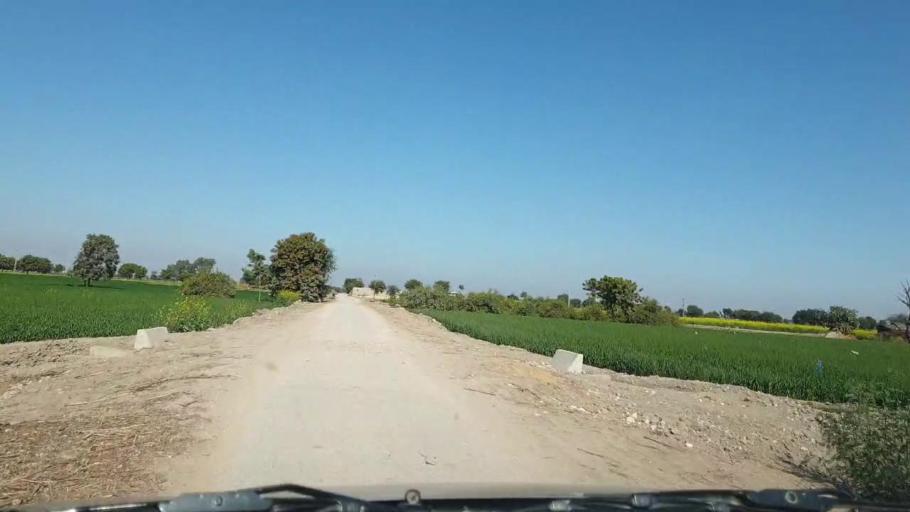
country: PK
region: Sindh
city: Khadro
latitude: 26.1393
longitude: 68.8159
